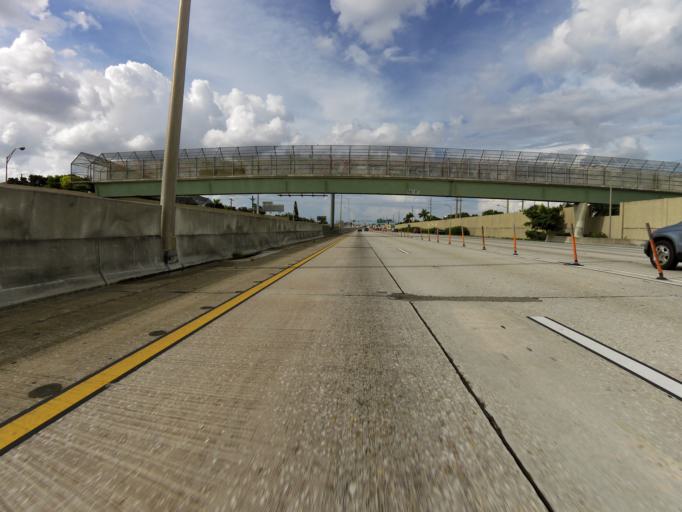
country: US
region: Florida
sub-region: Miami-Dade County
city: El Portal
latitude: 25.8348
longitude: -80.2060
